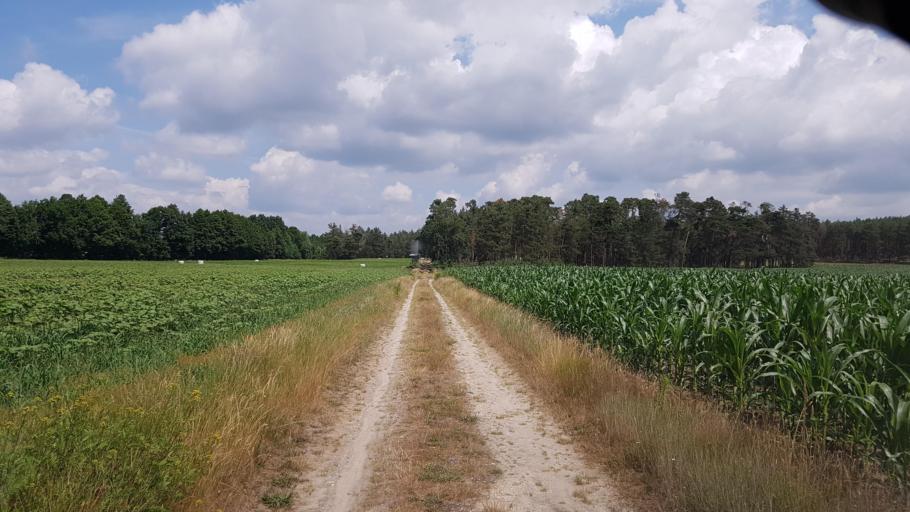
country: DE
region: Brandenburg
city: Crinitz
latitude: 51.7513
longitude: 13.8395
